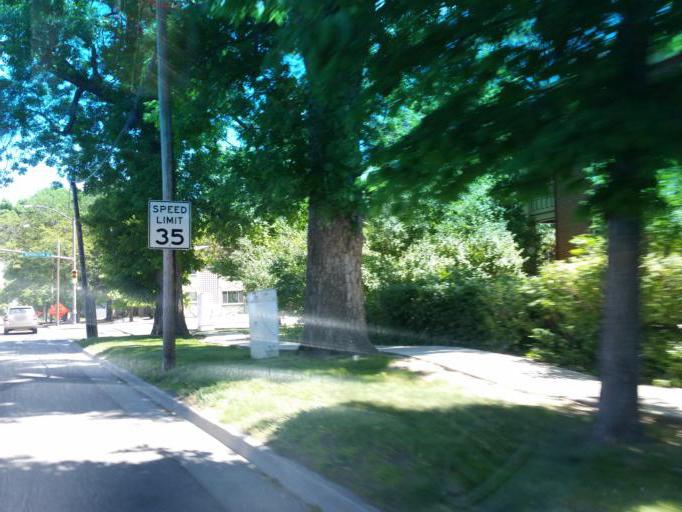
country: US
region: Colorado
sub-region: Larimer County
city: Fort Collins
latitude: 40.5814
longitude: -105.0762
